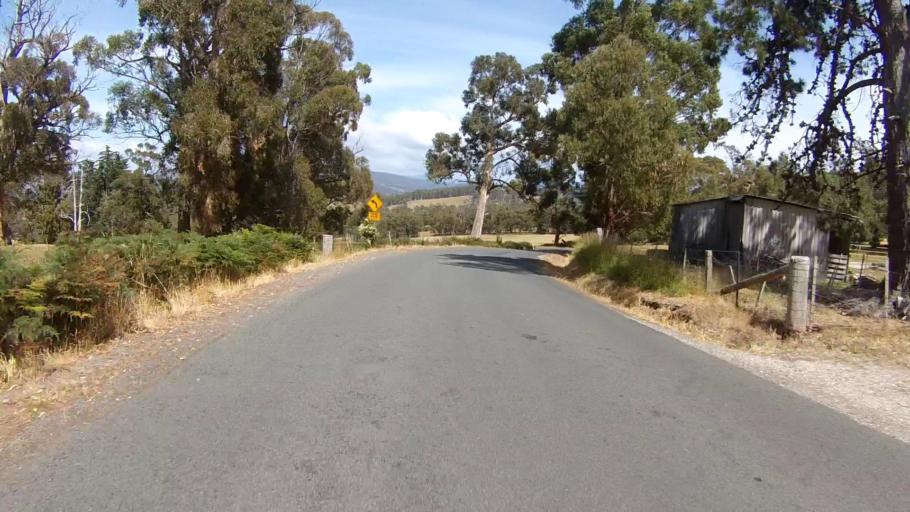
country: AU
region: Tasmania
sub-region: Huon Valley
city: Cygnet
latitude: -43.2328
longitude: 147.1277
